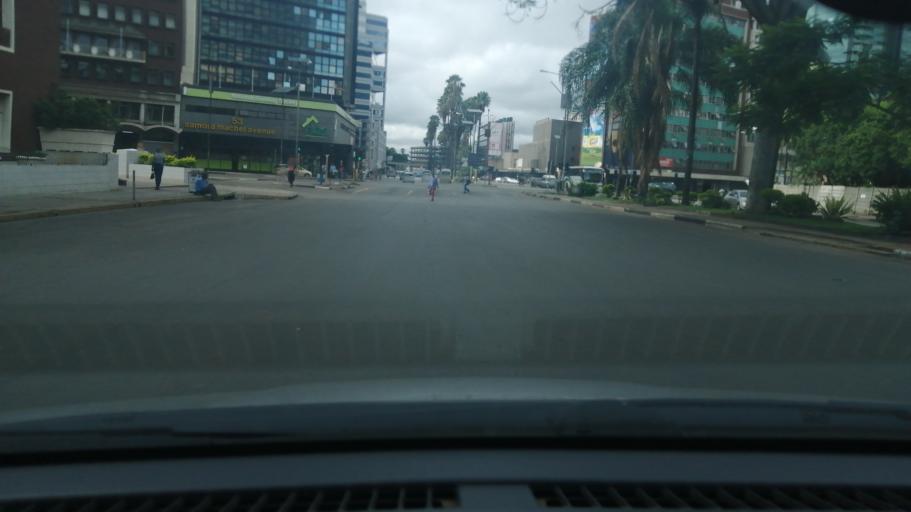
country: ZW
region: Harare
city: Harare
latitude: -17.8263
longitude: 31.0479
